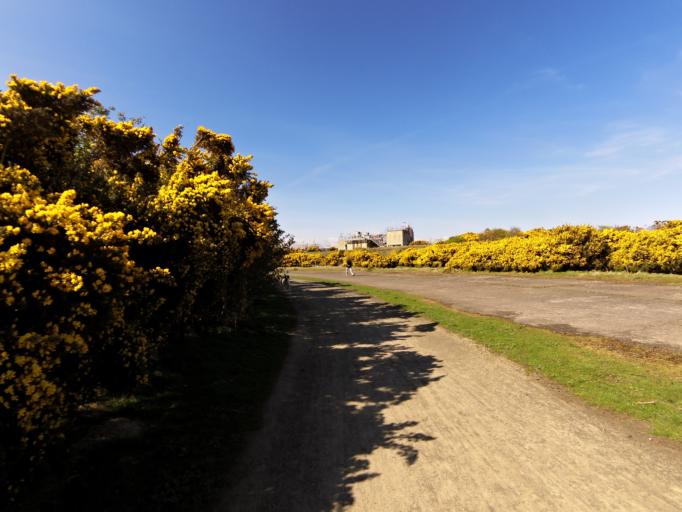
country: GB
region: Scotland
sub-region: Angus
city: Montrose
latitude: 56.7339
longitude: -2.4508
